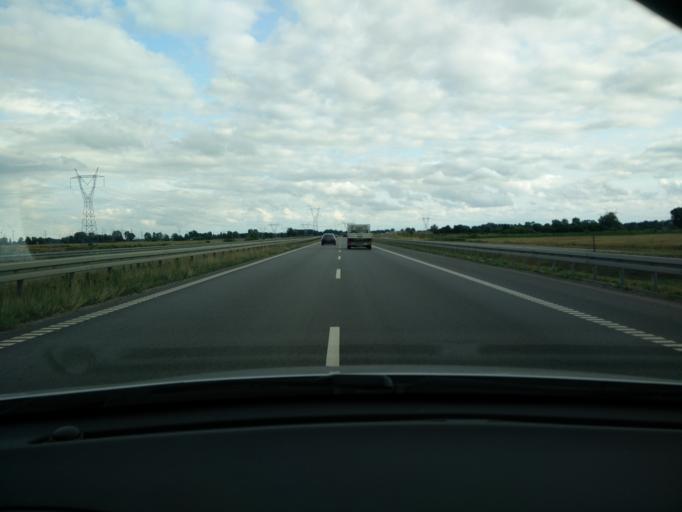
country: PL
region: Pomeranian Voivodeship
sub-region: Gdansk
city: Gdansk
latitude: 54.3312
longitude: 18.7041
